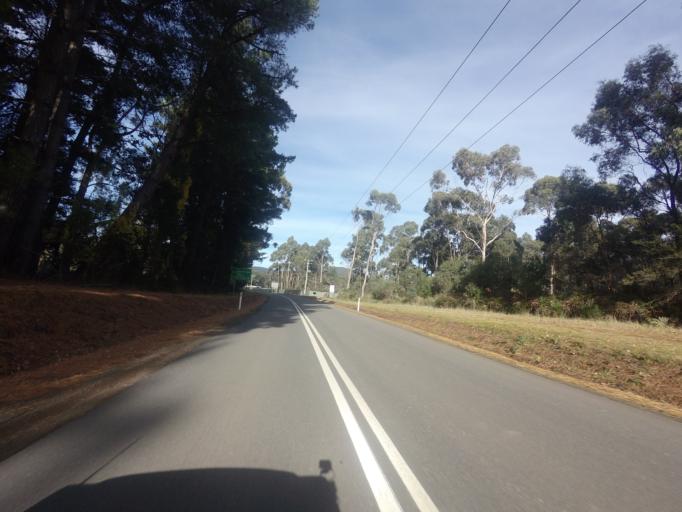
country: AU
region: Tasmania
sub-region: Clarence
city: Sandford
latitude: -43.0620
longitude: 147.8615
